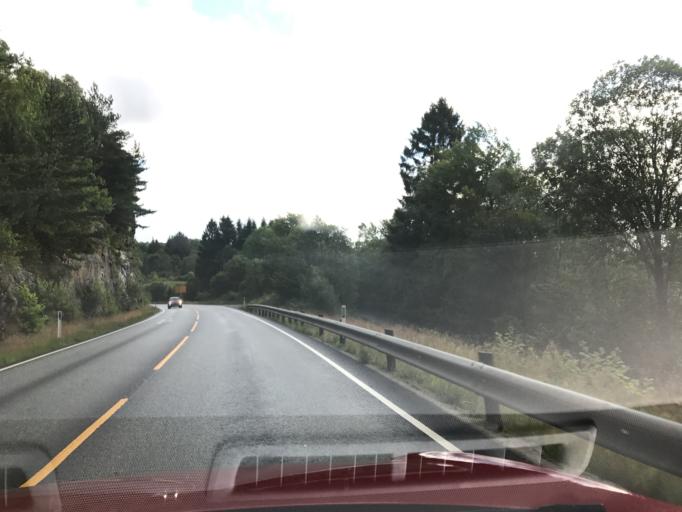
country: NO
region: Hordaland
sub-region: Sveio
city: Sveio
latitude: 59.5589
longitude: 5.4125
